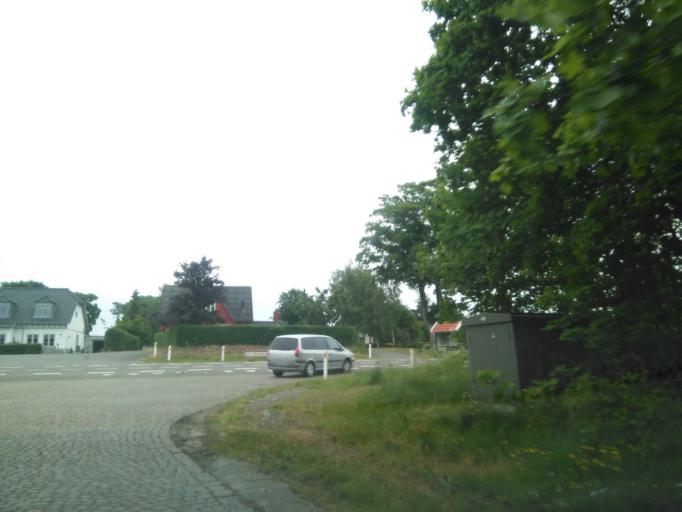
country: DK
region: Capital Region
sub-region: Bornholm Kommune
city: Akirkeby
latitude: 55.1104
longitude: 14.9114
